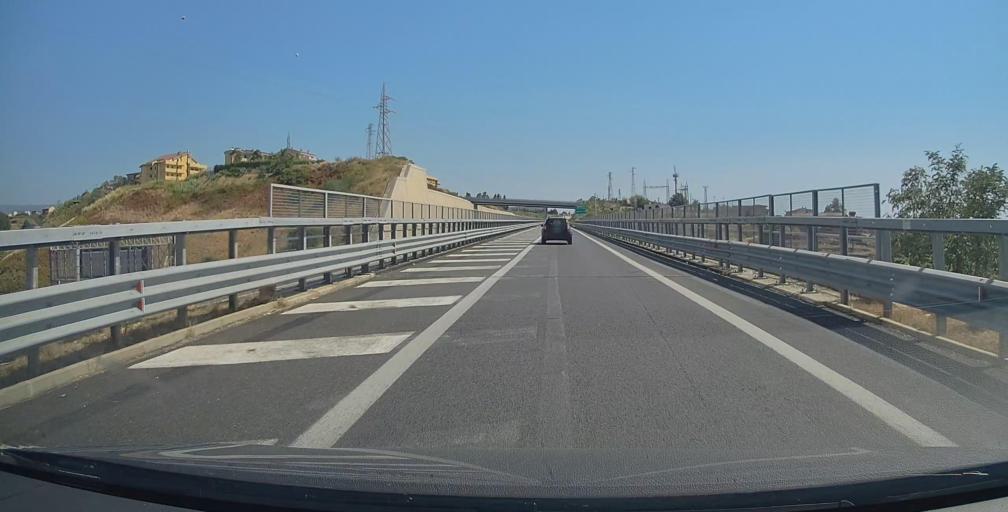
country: IT
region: Calabria
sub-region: Provincia di Reggio Calabria
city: Campo Calabro
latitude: 38.2205
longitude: 15.6477
